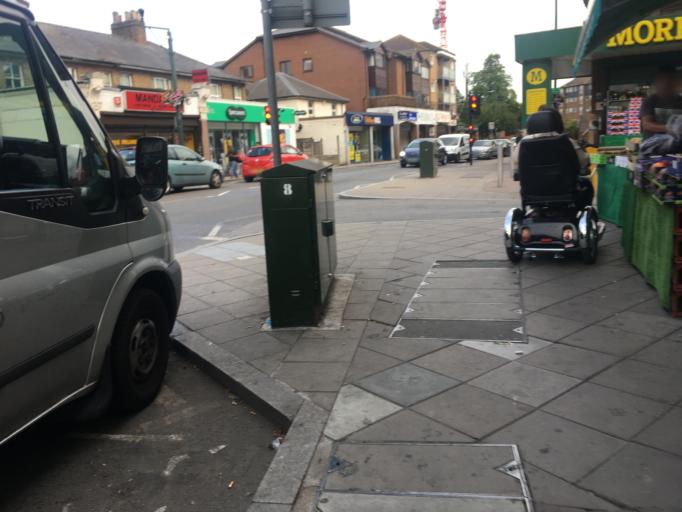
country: GB
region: England
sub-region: Greater London
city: West Drayton
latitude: 51.5124
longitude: -0.4726
